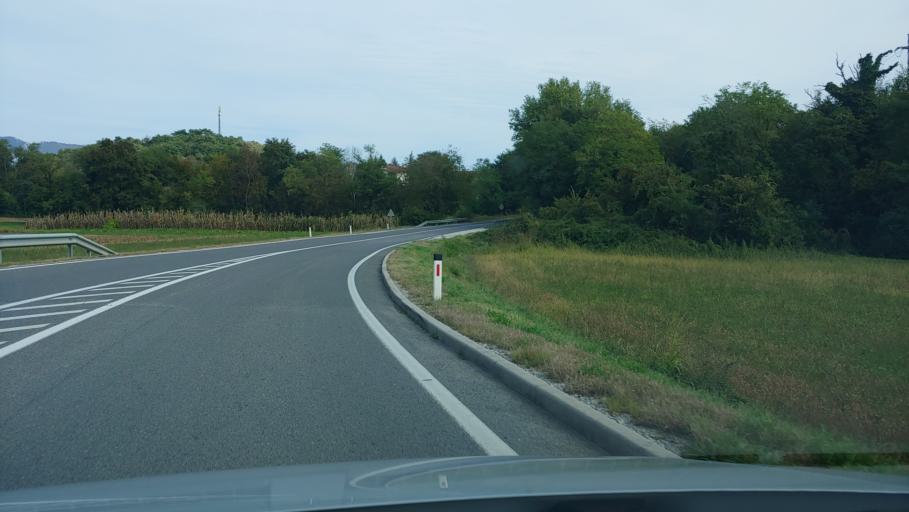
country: SI
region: Ajdovscina
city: Lokavec
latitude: 45.8856
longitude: 13.8333
